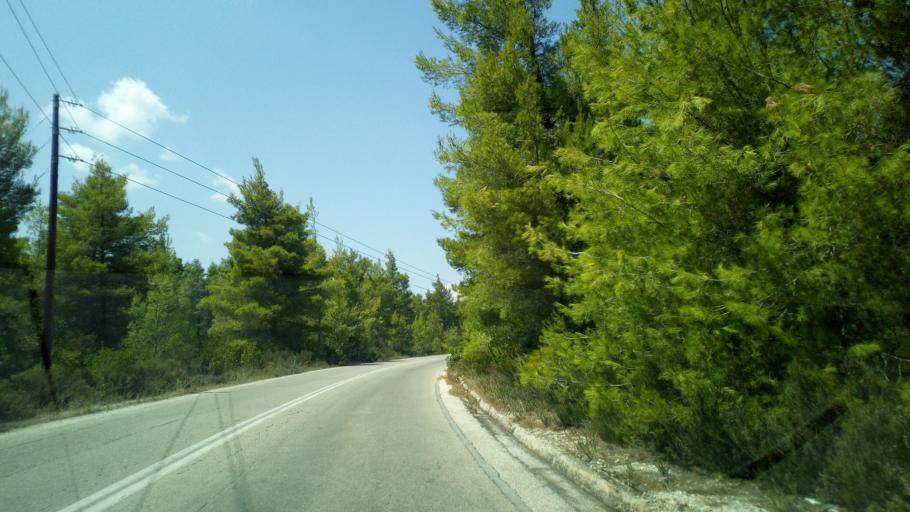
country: GR
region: Central Macedonia
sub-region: Nomos Chalkidikis
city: Sarti
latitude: 40.1308
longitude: 23.9287
